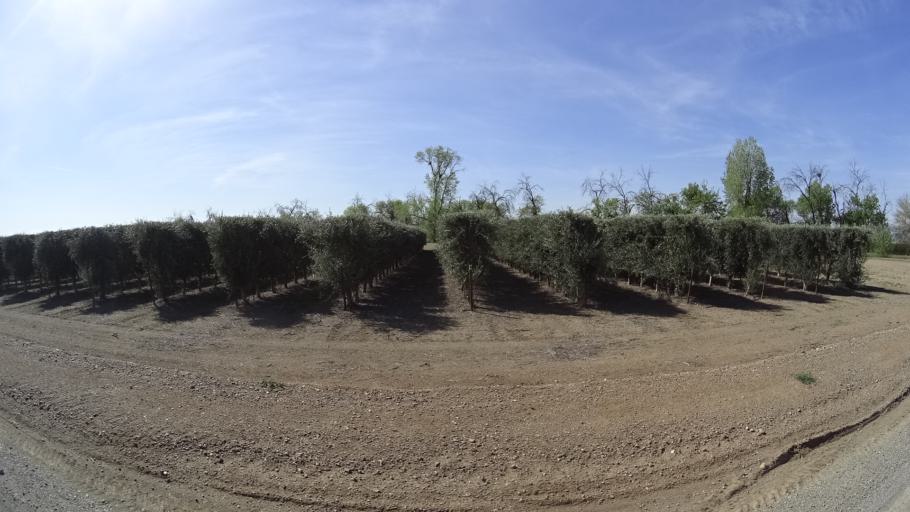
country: US
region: California
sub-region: Glenn County
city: Willows
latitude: 39.6117
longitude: -122.2594
